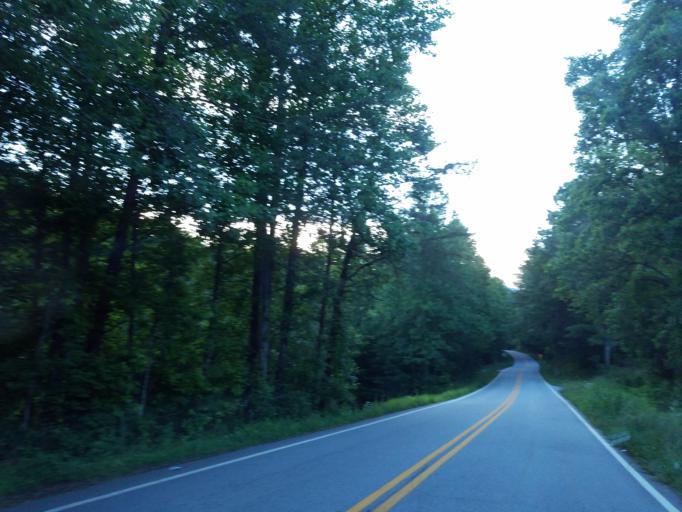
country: US
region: Georgia
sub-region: Lumpkin County
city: Dahlonega
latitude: 34.5888
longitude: -83.9707
